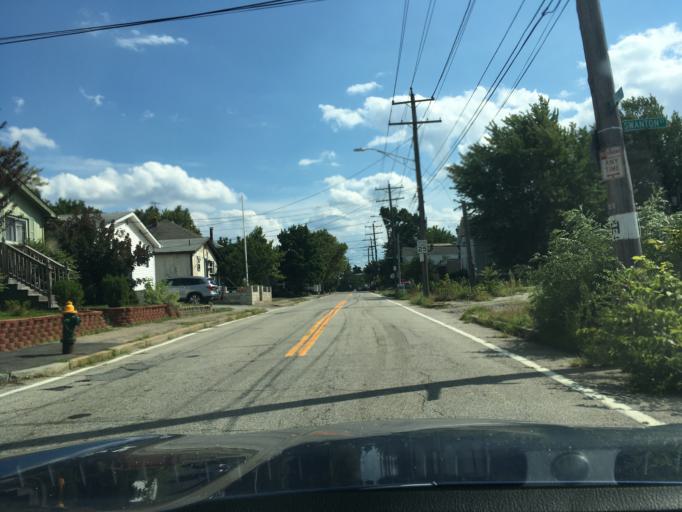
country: US
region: Rhode Island
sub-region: Providence County
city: Cranston
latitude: 41.7923
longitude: -71.4375
